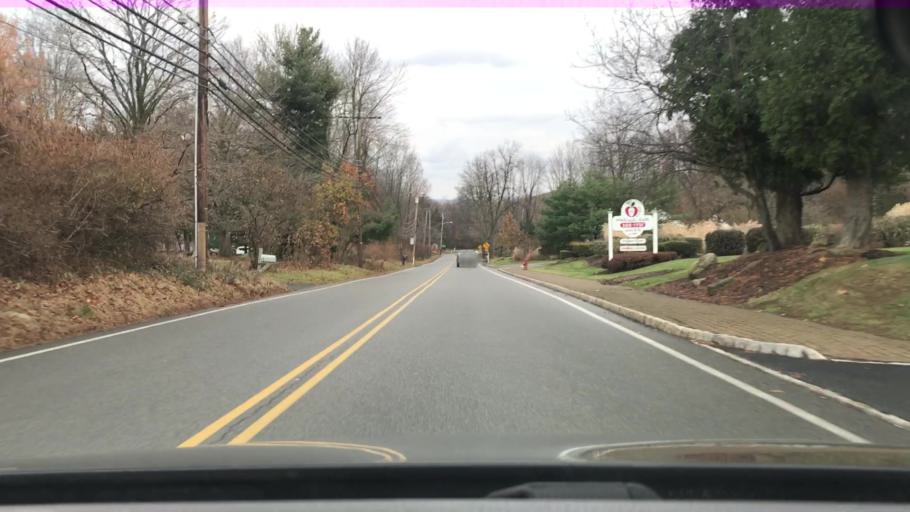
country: US
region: New Jersey
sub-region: Morris County
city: Randolph
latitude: 40.8488
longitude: -74.5615
